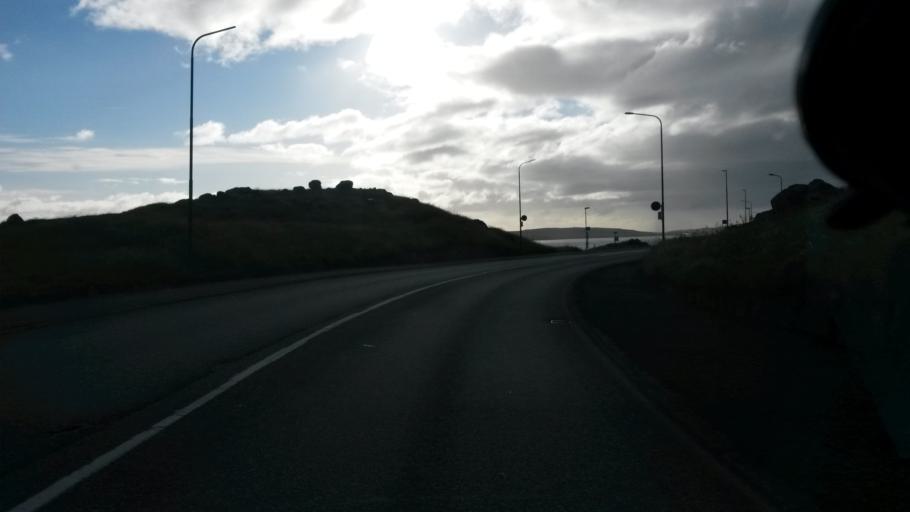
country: FO
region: Streymoy
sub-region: Torshavn
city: Torshavn
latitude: 62.0241
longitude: -6.7644
